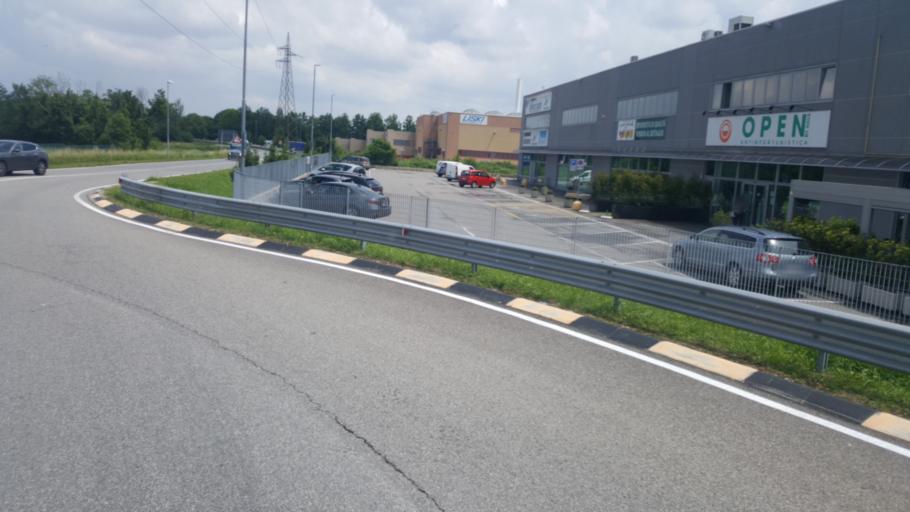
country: IT
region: Lombardy
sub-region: Provincia di Bergamo
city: Grignano
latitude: 45.6137
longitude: 9.5457
